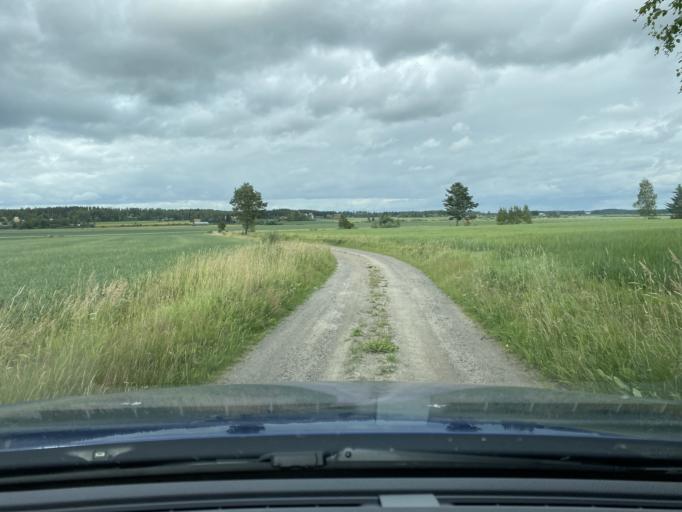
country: FI
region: Pirkanmaa
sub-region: Lounais-Pirkanmaa
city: Punkalaidun
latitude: 61.1001
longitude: 23.1158
